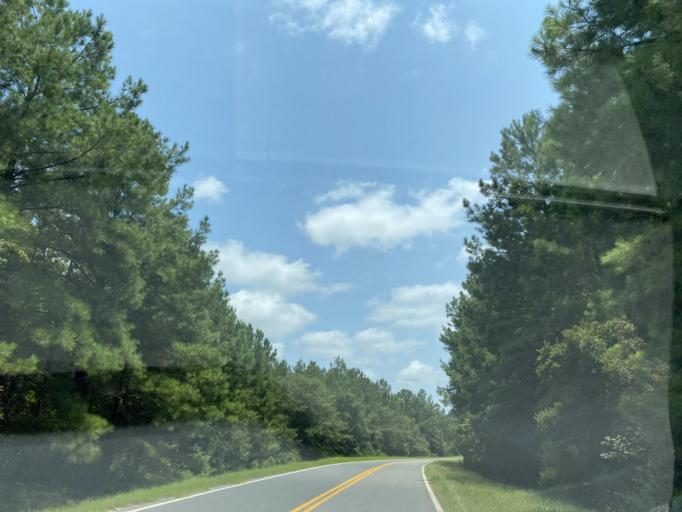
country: US
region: Georgia
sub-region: Telfair County
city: Lumber City
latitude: 31.9637
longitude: -82.7021
